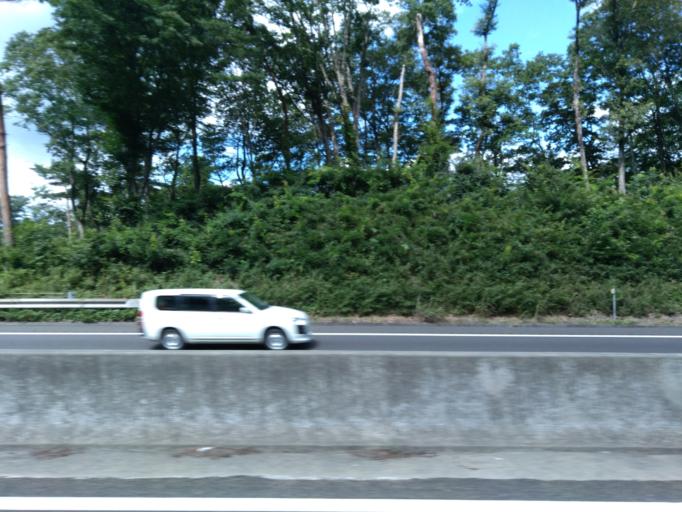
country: JP
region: Miyagi
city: Sendai-shi
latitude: 38.2997
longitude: 140.8090
